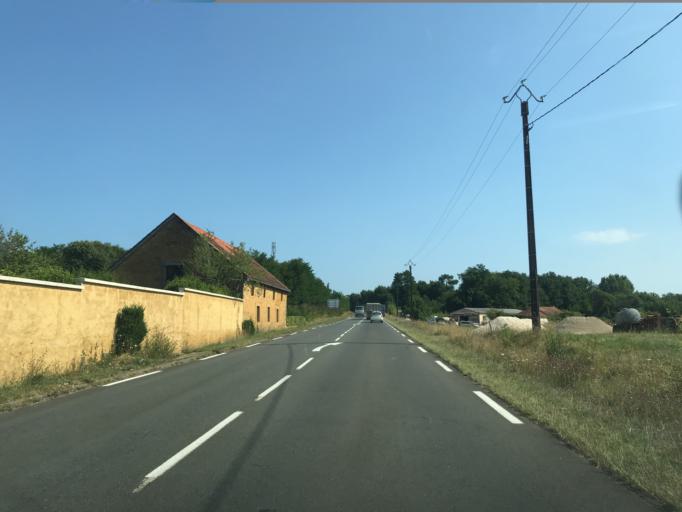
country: FR
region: Aquitaine
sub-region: Departement de la Dordogne
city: Sarlat-la-Caneda
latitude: 44.9882
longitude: 1.2406
